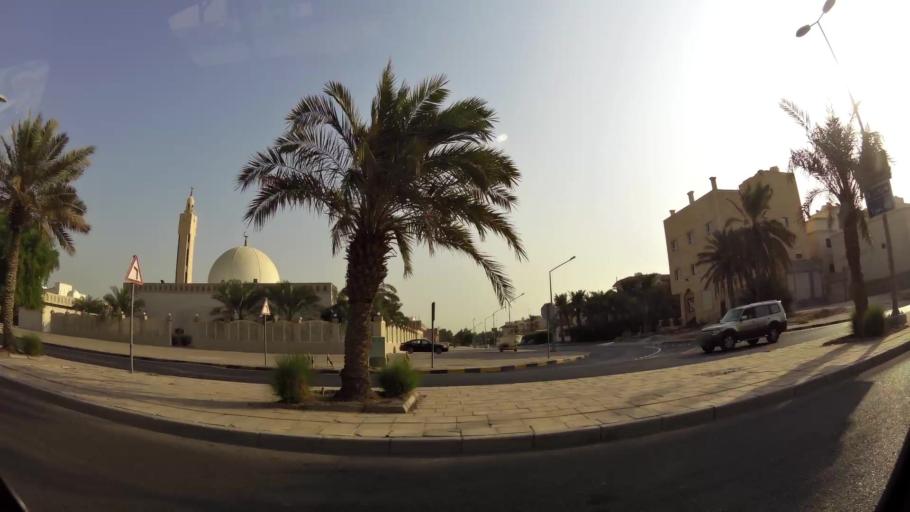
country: KW
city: Bayan
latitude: 29.3062
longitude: 48.0519
